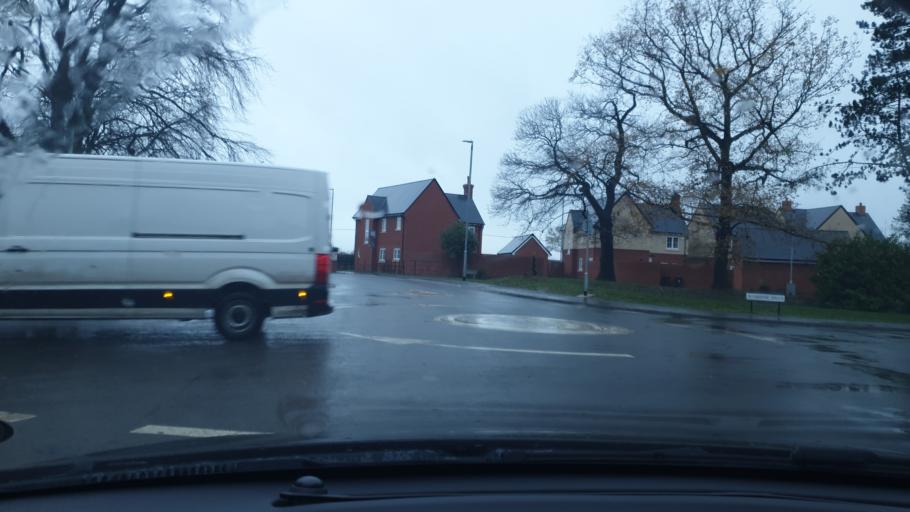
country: GB
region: England
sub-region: Essex
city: Great Horkesley
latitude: 51.9199
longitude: 0.8933
